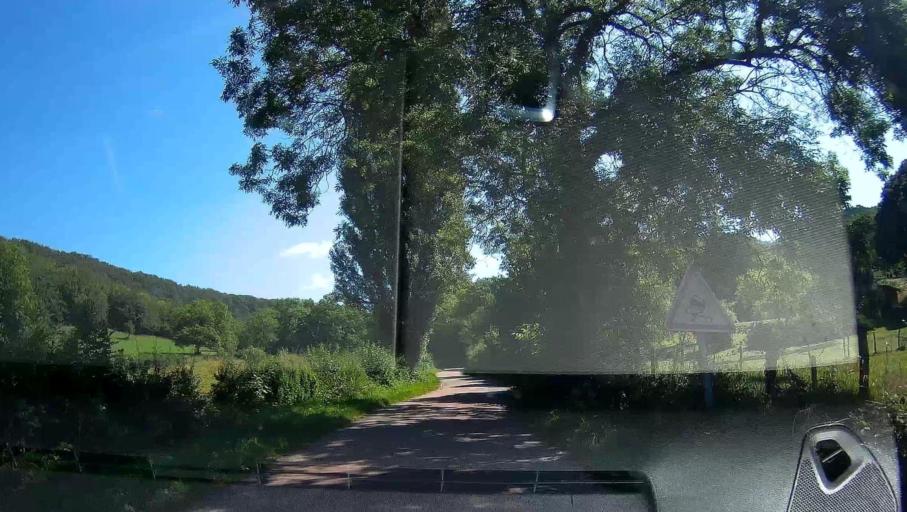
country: FR
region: Bourgogne
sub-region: Departement de la Cote-d'Or
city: Nolay
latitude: 46.9782
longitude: 4.6457
